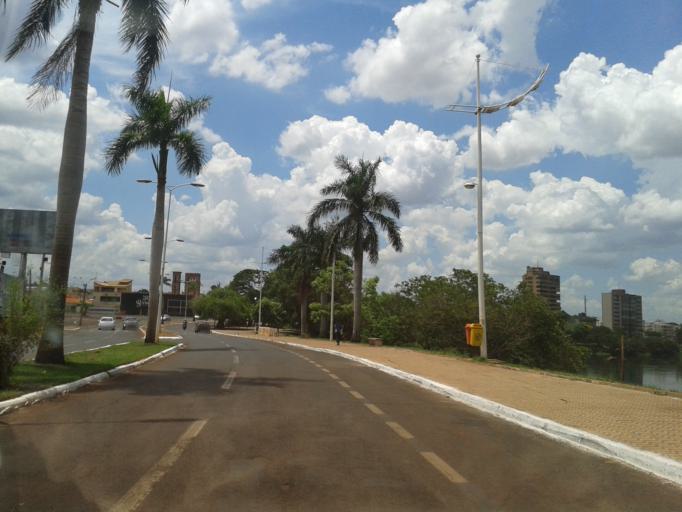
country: BR
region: Goias
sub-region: Itumbiara
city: Itumbiara
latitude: -18.4173
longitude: -49.2133
